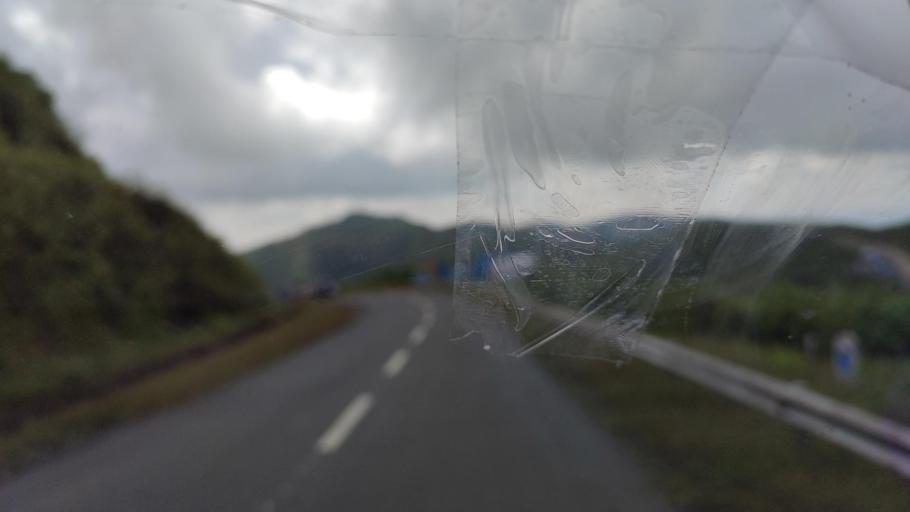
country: MM
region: Magway
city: Minbu
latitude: 19.8349
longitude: 94.2890
